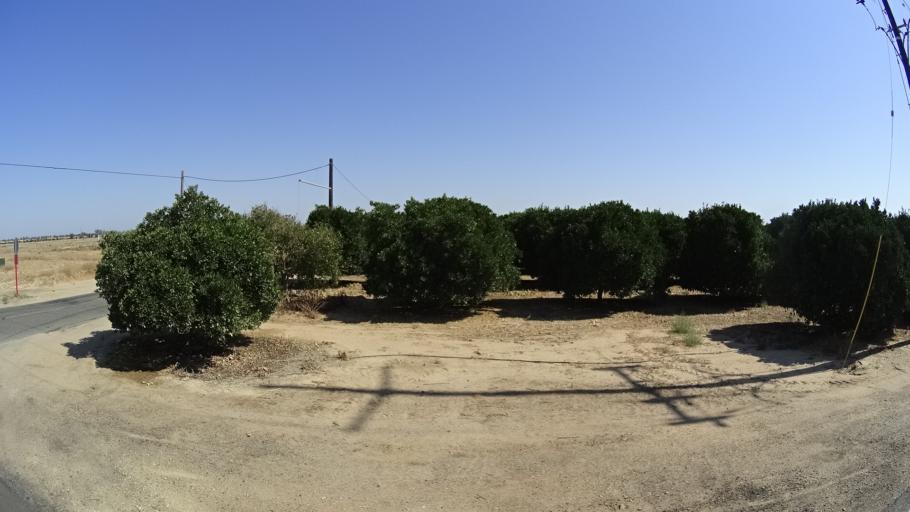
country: US
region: California
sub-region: Fresno County
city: Sunnyside
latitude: 36.7076
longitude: -119.6728
